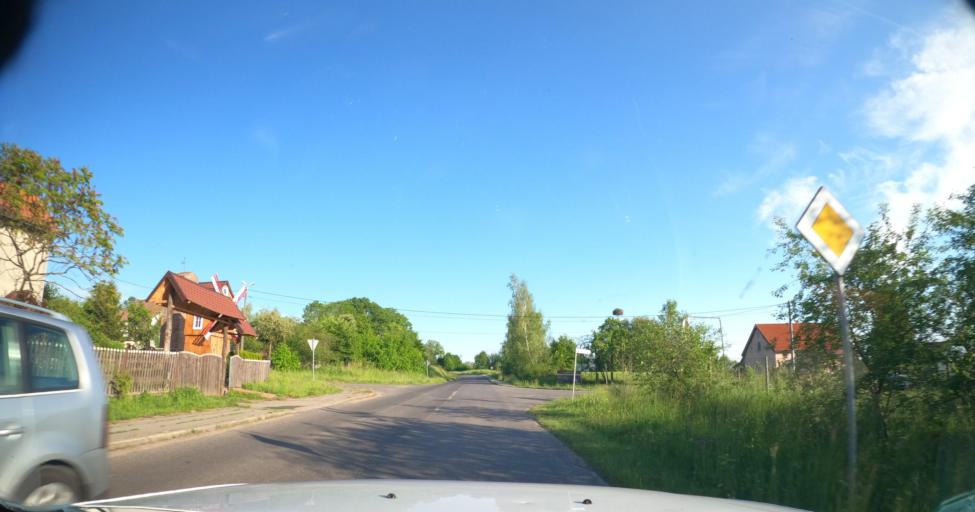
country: PL
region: Warmian-Masurian Voivodeship
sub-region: Powiat braniewski
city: Braniewo
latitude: 54.2698
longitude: 19.9378
